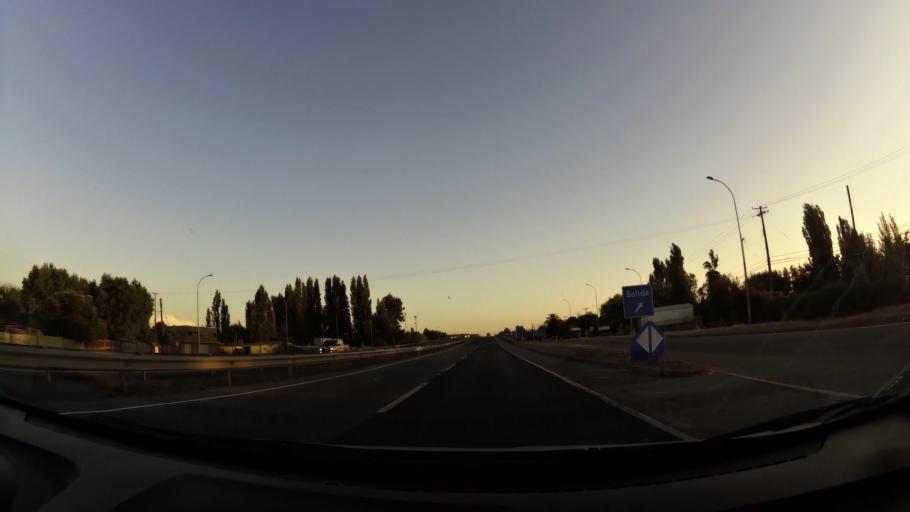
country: CL
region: Maule
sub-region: Provincia de Linares
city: San Javier
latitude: -35.5986
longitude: -71.7067
